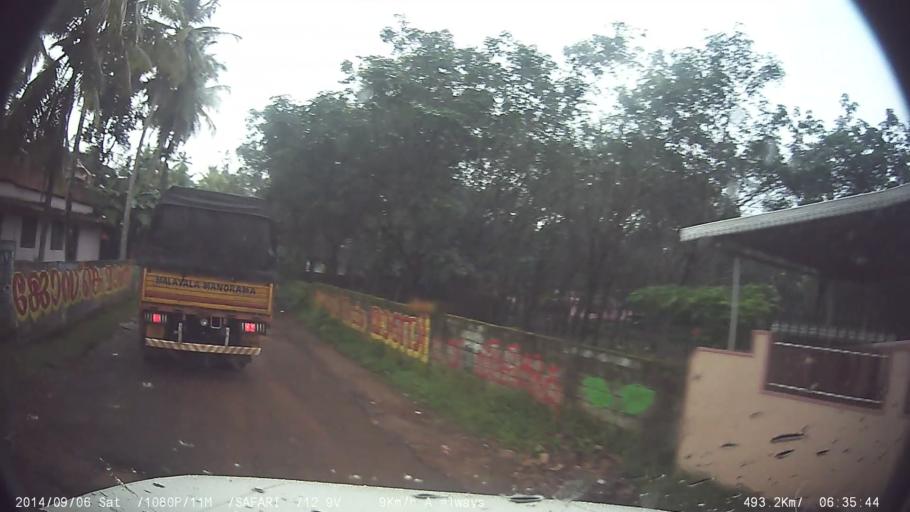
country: IN
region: Kerala
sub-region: Kottayam
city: Vaikam
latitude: 9.7863
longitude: 76.4544
